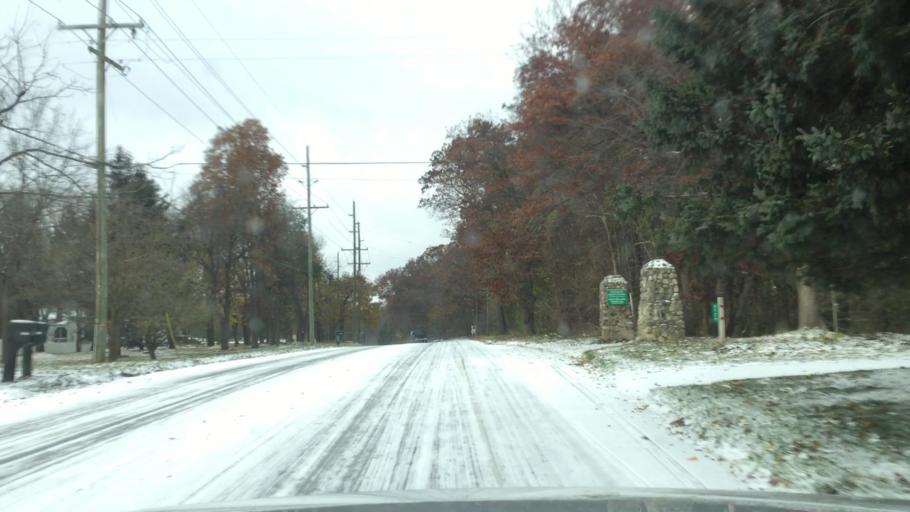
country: US
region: Michigan
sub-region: Livingston County
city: Brighton
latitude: 42.5285
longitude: -83.8219
